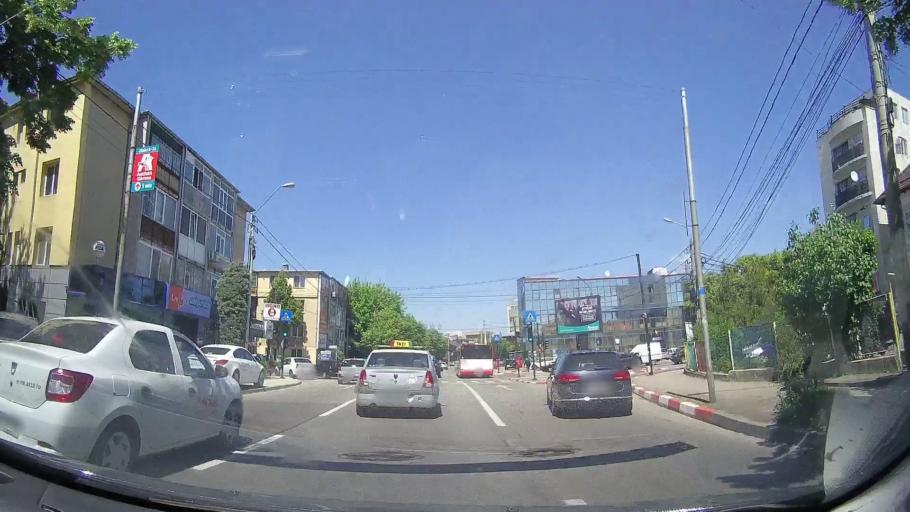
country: RO
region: Arges
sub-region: Comuna Albestii de Arges
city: Pitesti
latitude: 44.8605
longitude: 24.8665
